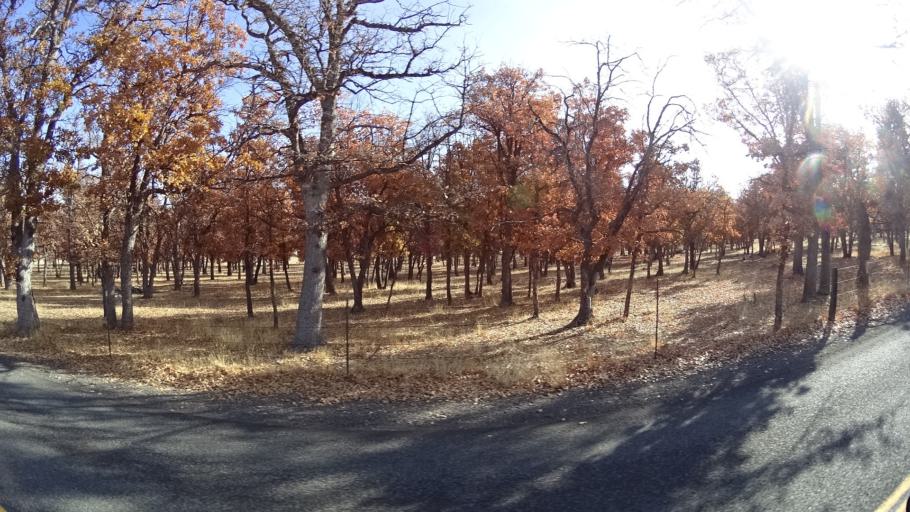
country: US
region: California
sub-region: Siskiyou County
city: Montague
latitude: 41.6485
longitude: -122.5830
